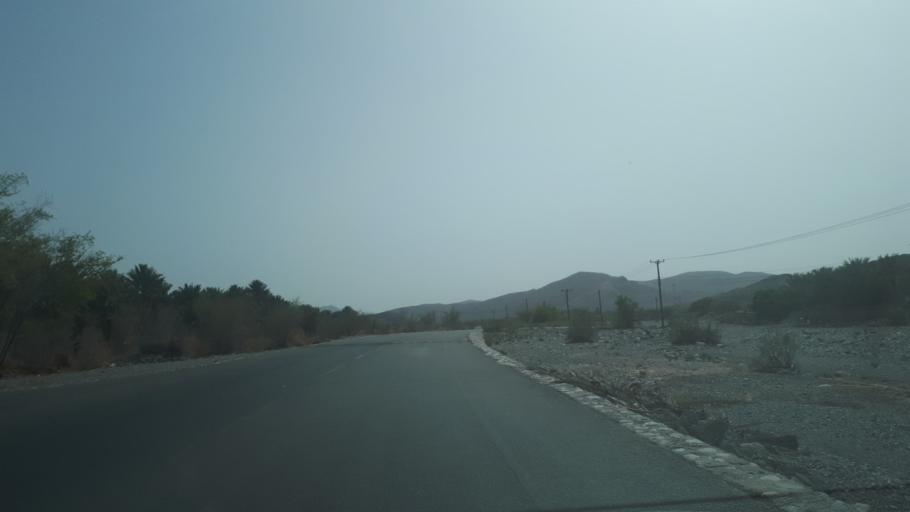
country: OM
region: Muhafazat ad Dakhiliyah
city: Bahla'
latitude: 23.2130
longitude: 56.9634
